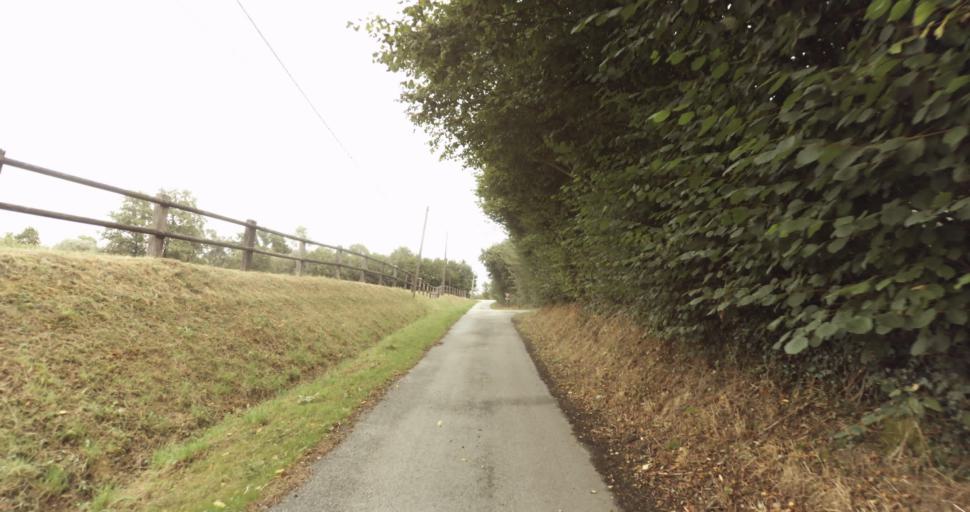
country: FR
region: Lower Normandy
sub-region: Departement de l'Orne
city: Sainte-Gauburge-Sainte-Colombe
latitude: 48.7012
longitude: 0.4374
